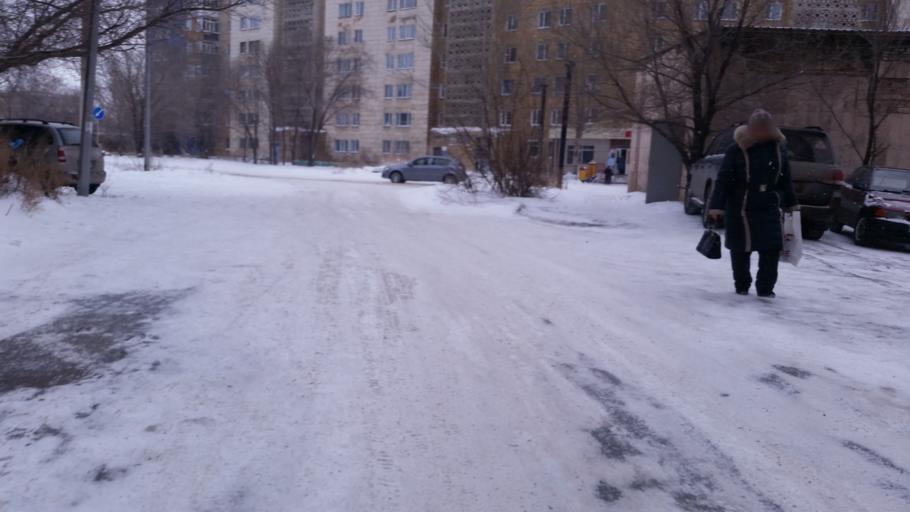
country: KZ
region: Qaraghandy
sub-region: Qaraghandy Qalasy
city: Karagandy
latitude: 49.7736
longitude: 73.1541
